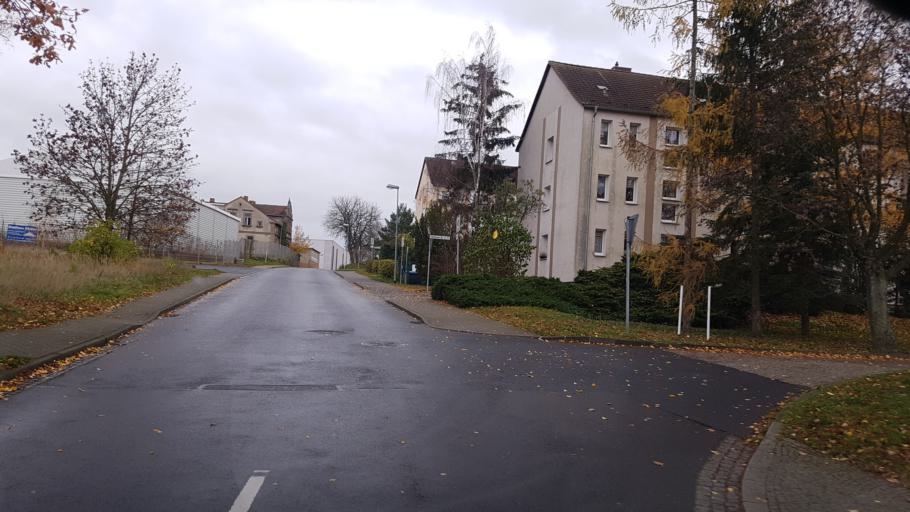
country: DE
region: Brandenburg
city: Ortrand
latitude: 51.3732
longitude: 13.7593
